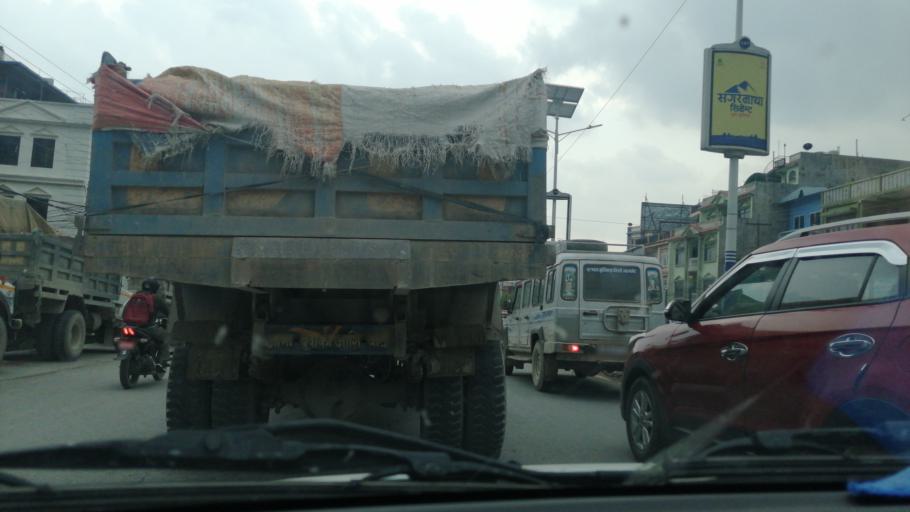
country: NP
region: Western Region
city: Butwal
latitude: 27.7061
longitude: 83.4673
